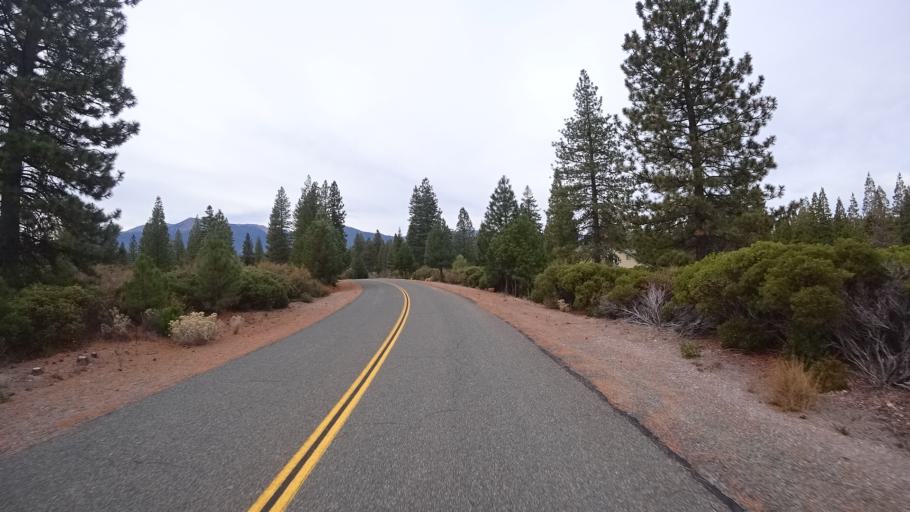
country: US
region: California
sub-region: Siskiyou County
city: Weed
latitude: 41.4082
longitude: -122.3664
